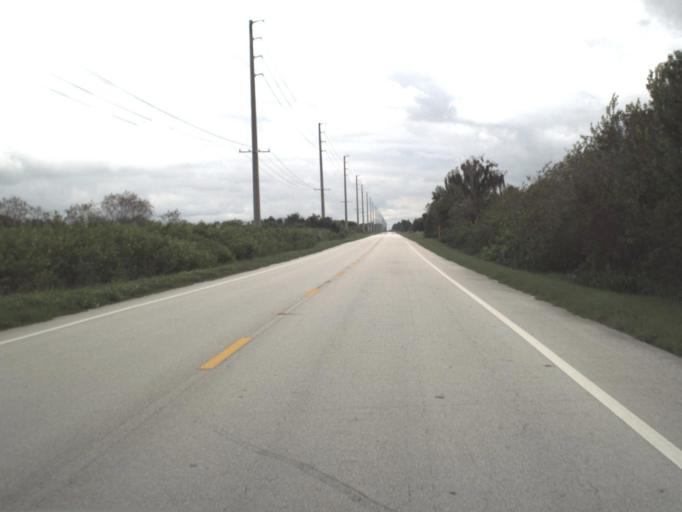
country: US
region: Florida
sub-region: Hardee County
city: Bowling Green
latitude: 27.5950
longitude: -82.0046
